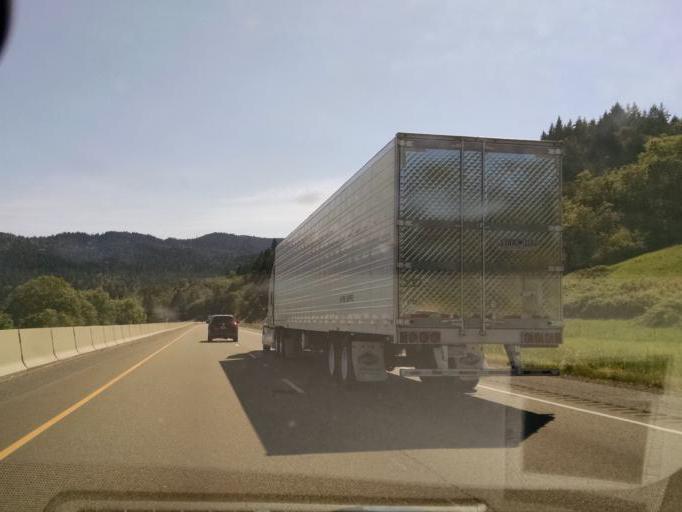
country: US
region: Oregon
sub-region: Douglas County
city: Myrtle Creek
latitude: 43.0458
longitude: -123.3323
